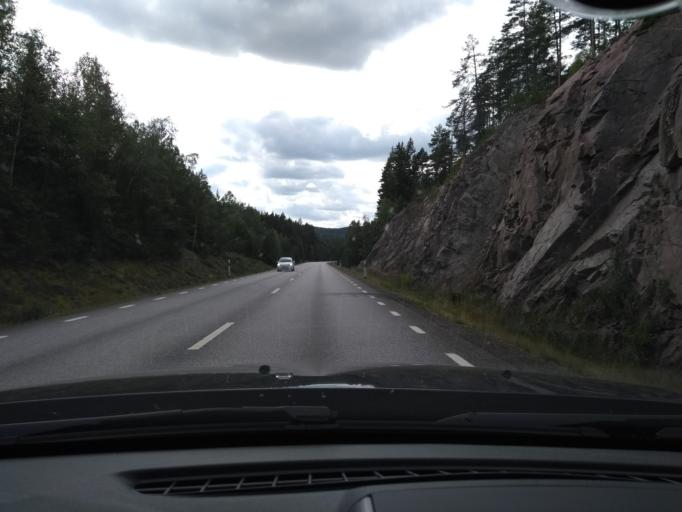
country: SE
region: Kalmar
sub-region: Vimmerby Kommun
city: Vimmerby
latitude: 57.6386
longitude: 15.7619
